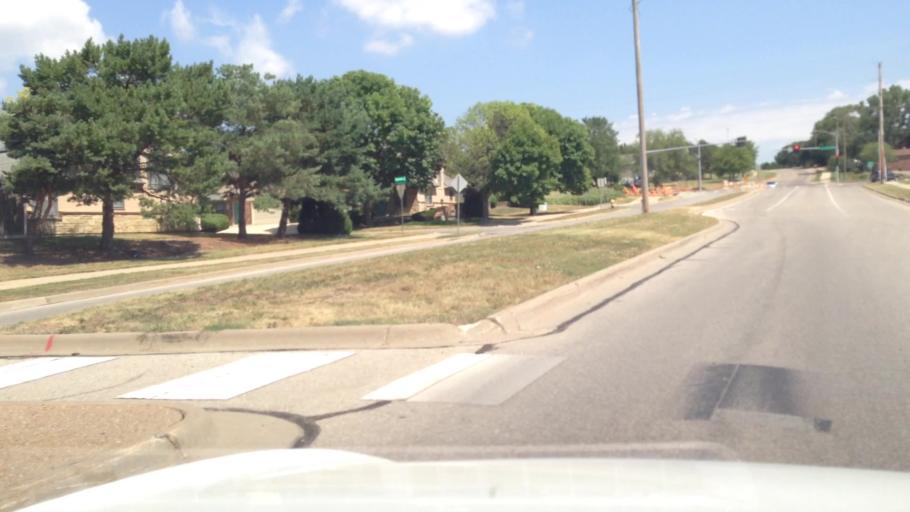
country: US
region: Kansas
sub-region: Douglas County
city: Lawrence
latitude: 38.9412
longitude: -95.2978
